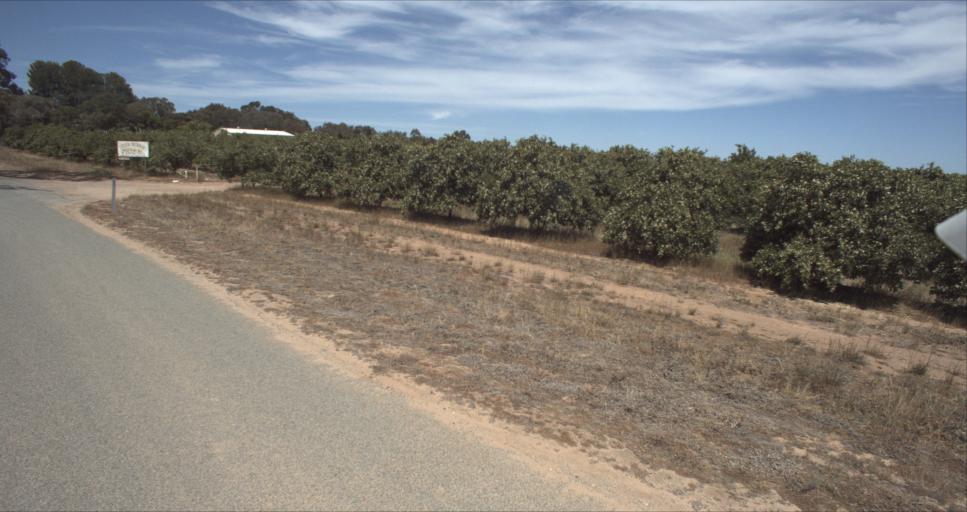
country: AU
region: New South Wales
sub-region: Leeton
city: Leeton
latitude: -34.6756
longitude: 146.4333
